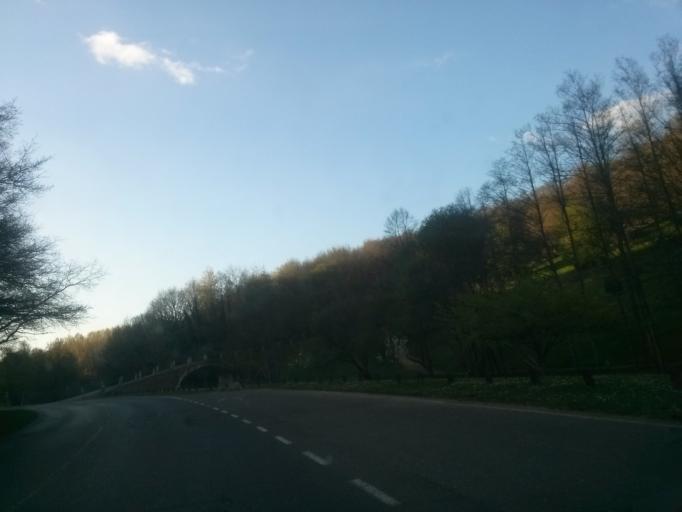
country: ES
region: Galicia
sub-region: Provincia de Lugo
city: Lugo
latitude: 43.0036
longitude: -7.5334
